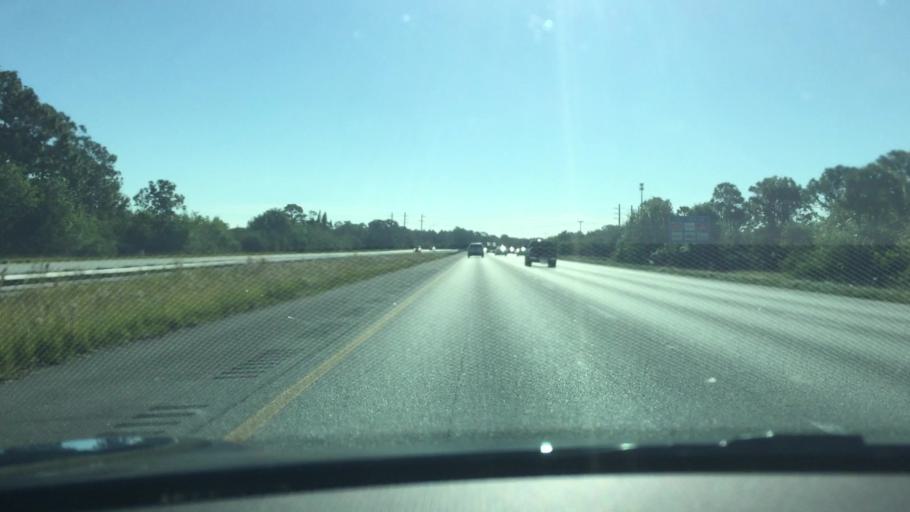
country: US
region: Florida
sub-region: Brevard County
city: West Melbourne
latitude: 28.0458
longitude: -80.6665
